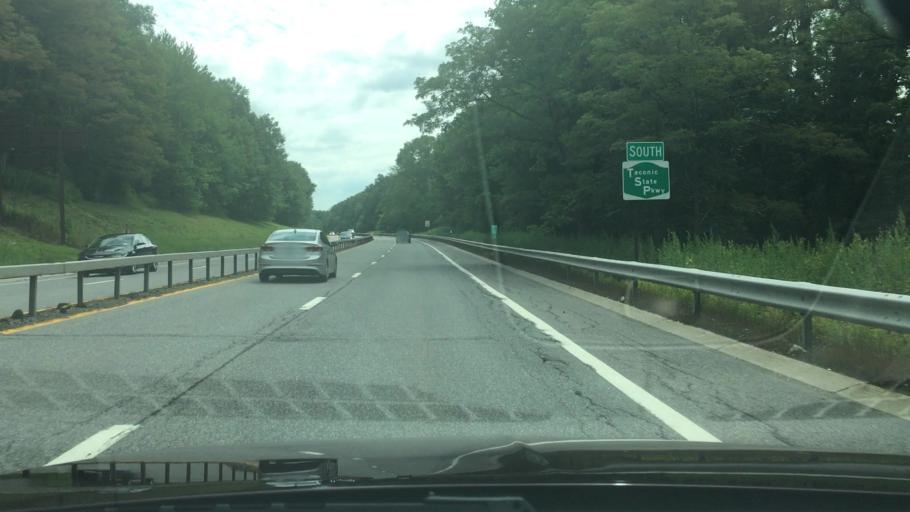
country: US
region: New York
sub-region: Westchester County
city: Shrub Oak
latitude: 41.3710
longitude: -73.8012
